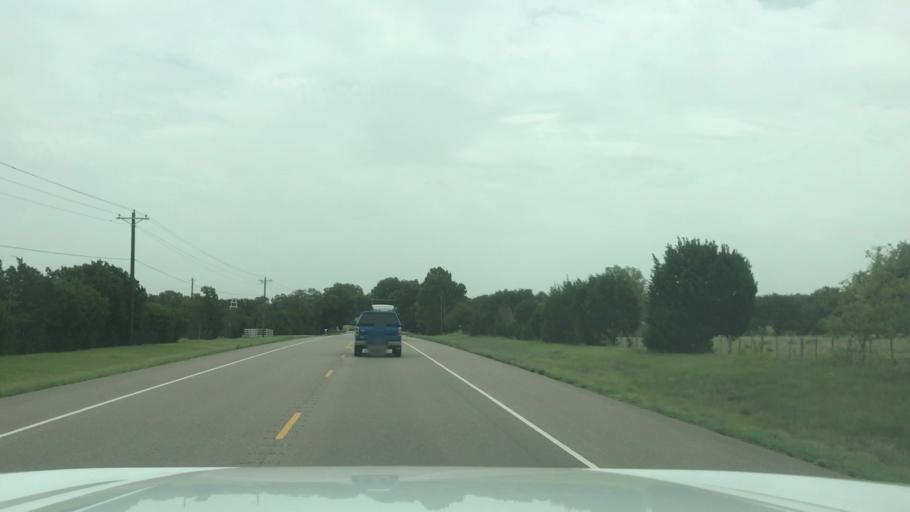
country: US
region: Texas
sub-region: Bosque County
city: Meridian
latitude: 31.9379
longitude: -97.7062
